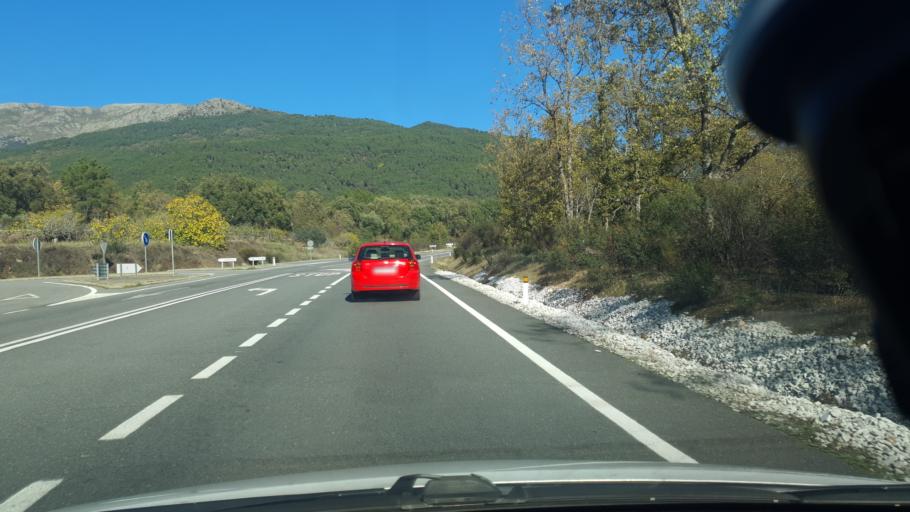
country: ES
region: Castille and Leon
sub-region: Provincia de Avila
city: Piedralaves
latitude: 40.3012
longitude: -4.7196
